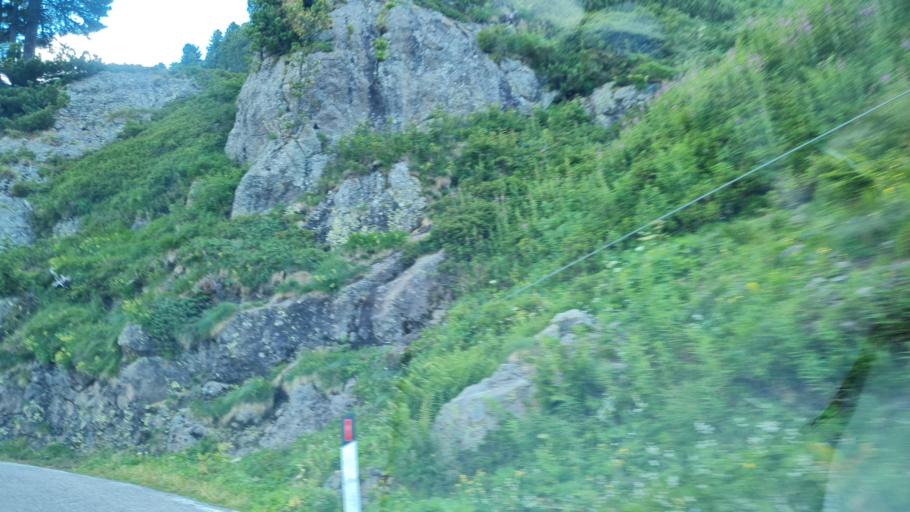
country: IT
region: Trentino-Alto Adige
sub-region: Provincia di Trento
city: Torcegno
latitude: 46.1695
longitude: 11.4441
